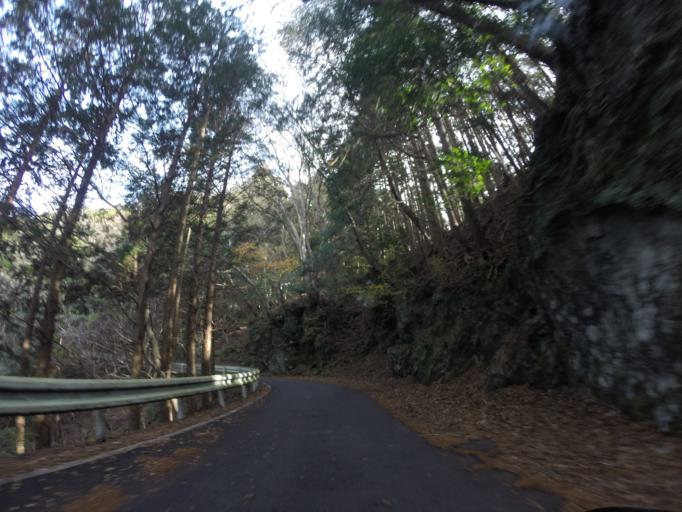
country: JP
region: Shizuoka
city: Heda
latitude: 34.8329
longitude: 138.8479
